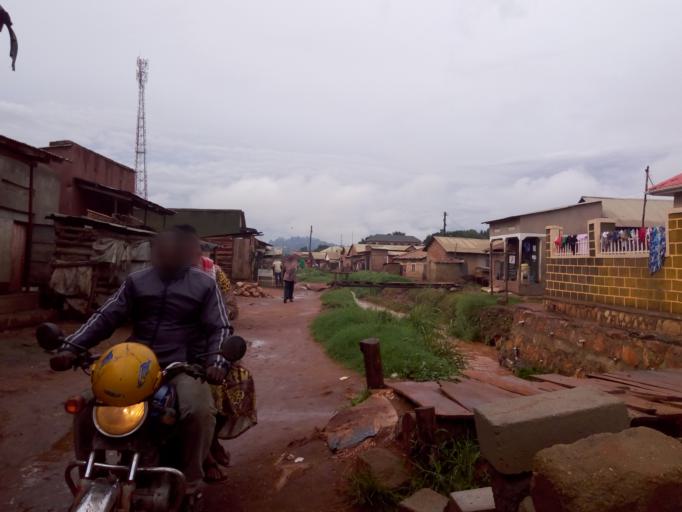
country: UG
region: Central Region
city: Kampala Central Division
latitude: 0.3398
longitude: 32.5584
